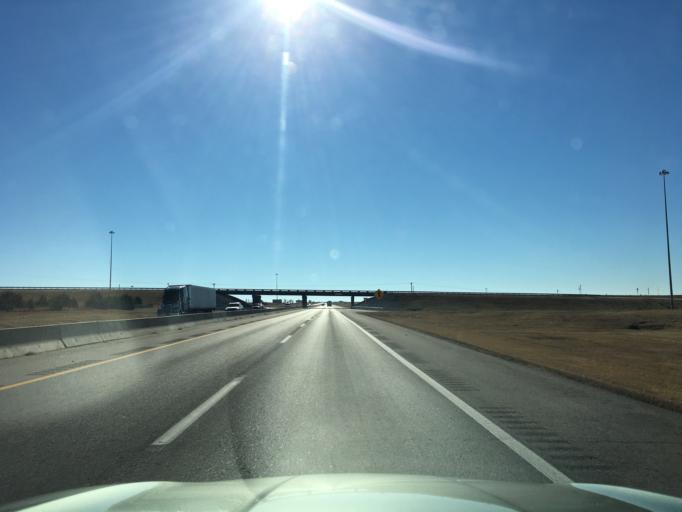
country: US
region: Kansas
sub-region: Sumner County
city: Wellington
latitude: 37.0594
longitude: -97.3385
